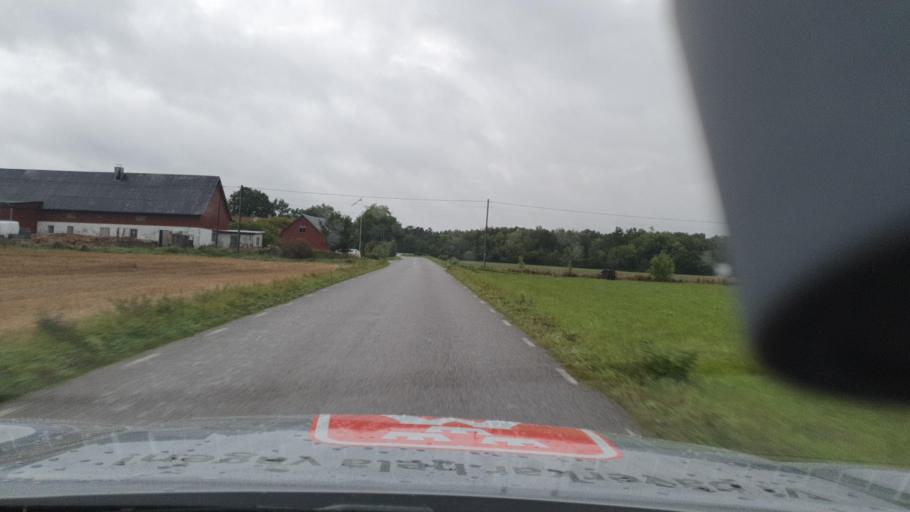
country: SE
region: Gotland
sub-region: Gotland
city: Visby
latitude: 57.7740
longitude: 18.4962
